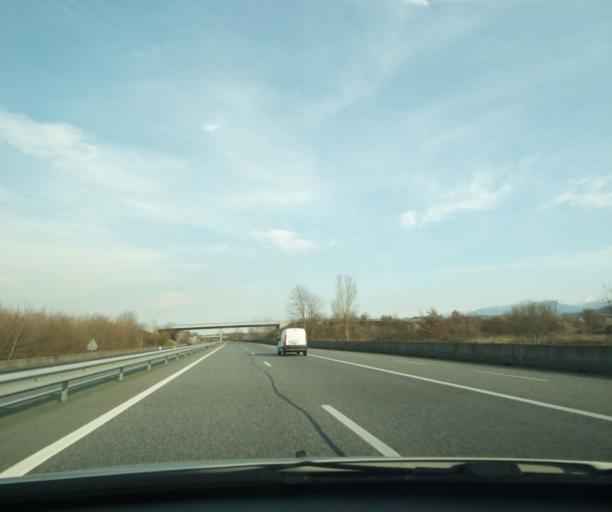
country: FR
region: Midi-Pyrenees
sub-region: Departement de la Haute-Garonne
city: Villeneuve-de-Riviere
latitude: 43.1142
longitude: 0.6643
